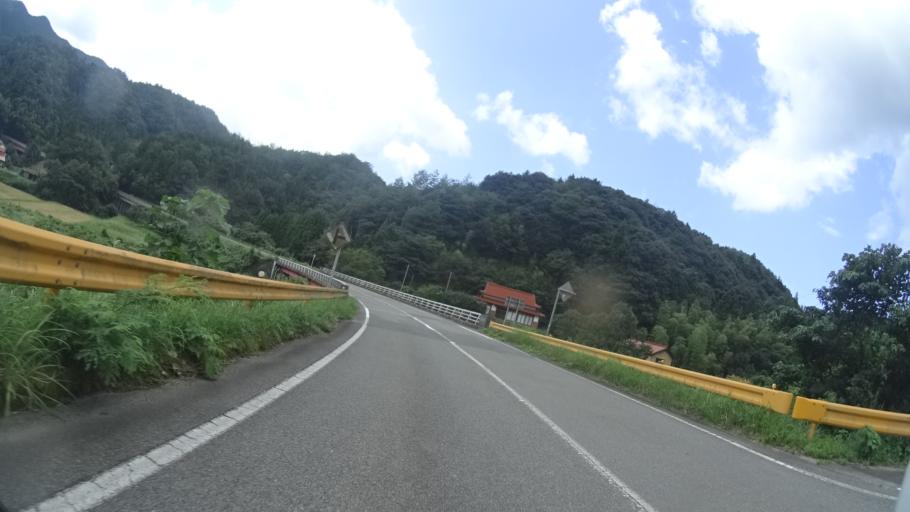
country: JP
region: Yamaguchi
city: Hagi
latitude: 34.5526
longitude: 131.6003
